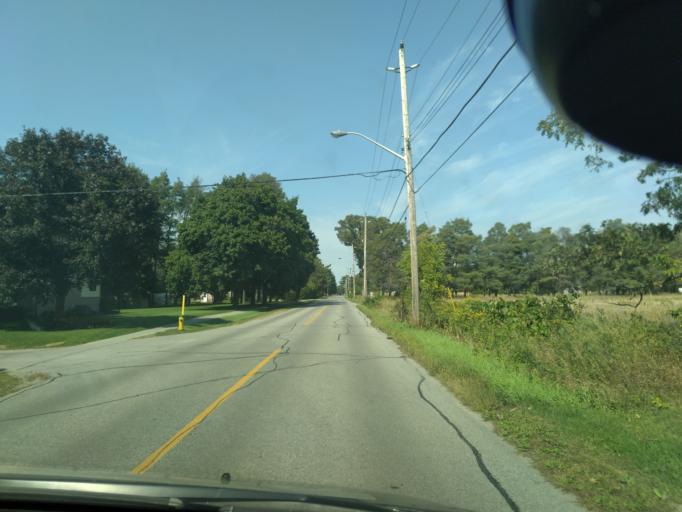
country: CA
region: Ontario
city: Newmarket
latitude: 44.1091
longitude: -79.5033
